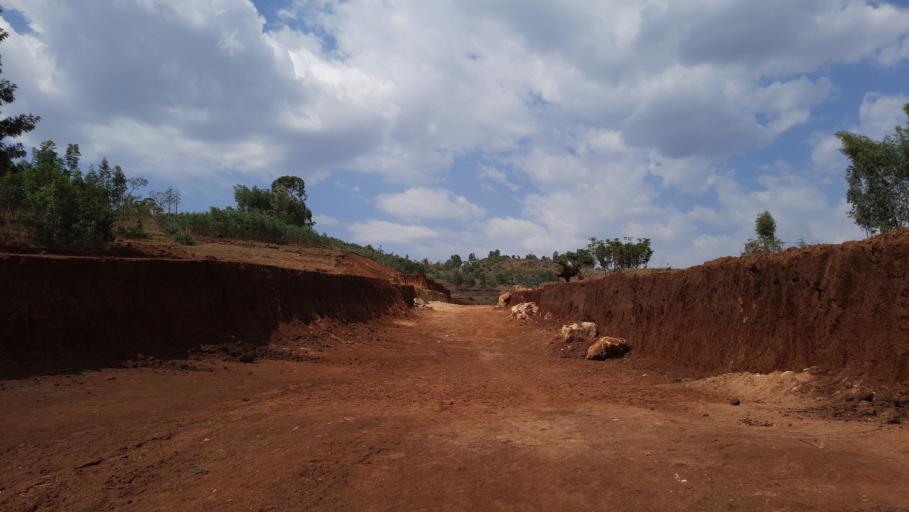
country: ET
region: Southern Nations, Nationalities, and People's Region
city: Areka
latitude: 7.2162
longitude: 37.2608
